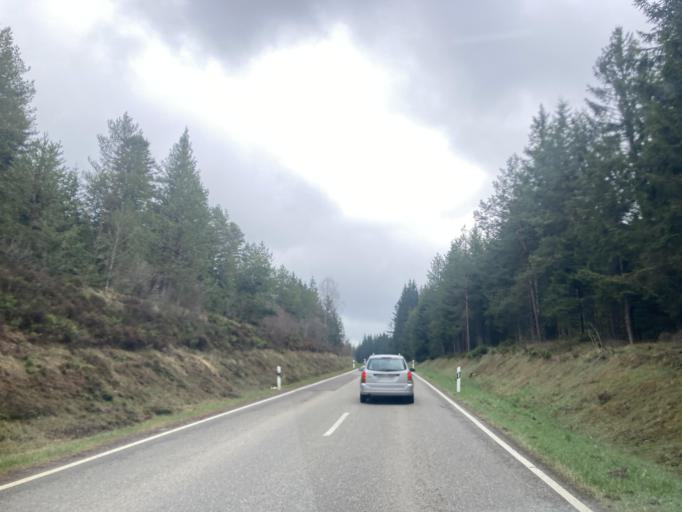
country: DE
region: Baden-Wuerttemberg
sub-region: Freiburg Region
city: Vohrenbach
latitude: 48.0368
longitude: 8.3403
